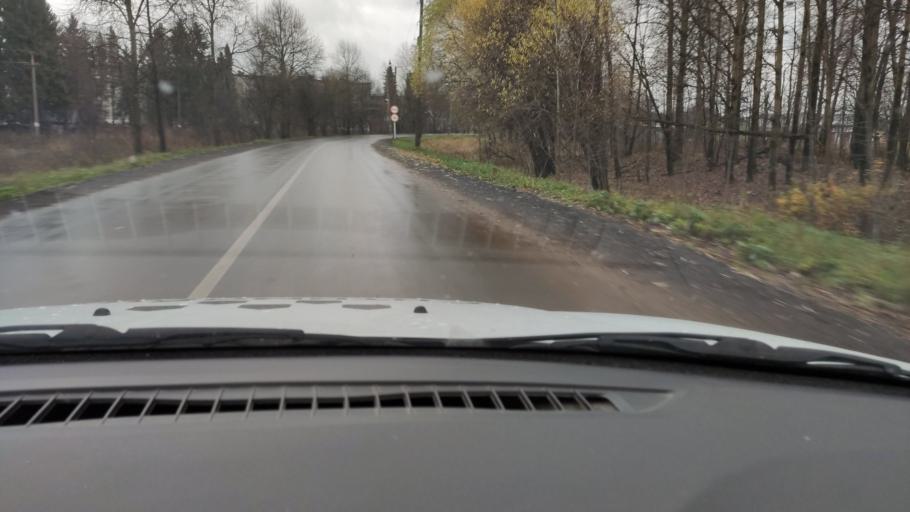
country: RU
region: Perm
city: Sylva
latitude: 58.0327
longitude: 56.7401
